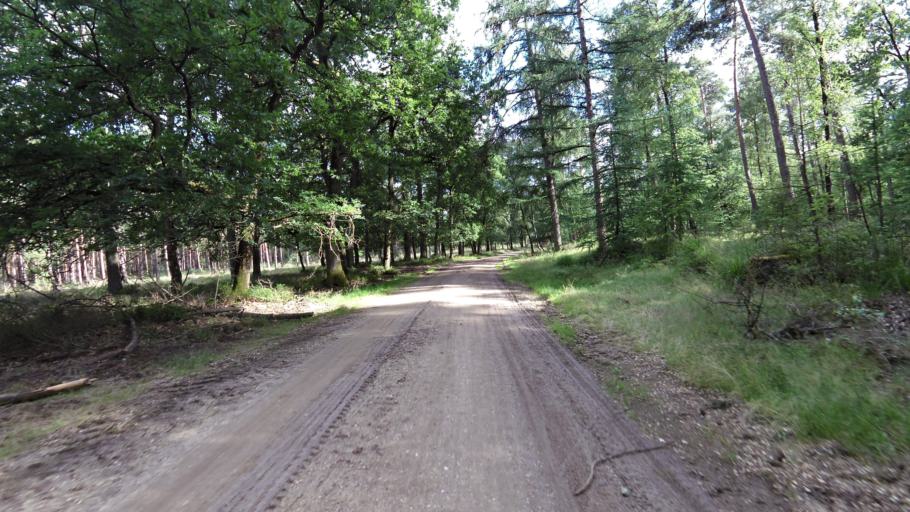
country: NL
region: Gelderland
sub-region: Gemeente Apeldoorn
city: Uddel
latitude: 52.2812
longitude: 5.8669
